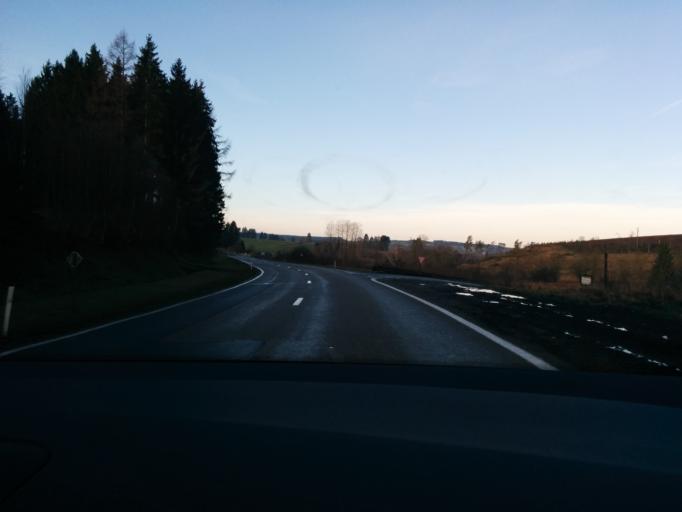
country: BE
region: Wallonia
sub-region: Province du Luxembourg
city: Gouvy
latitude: 50.2209
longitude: 5.9460
